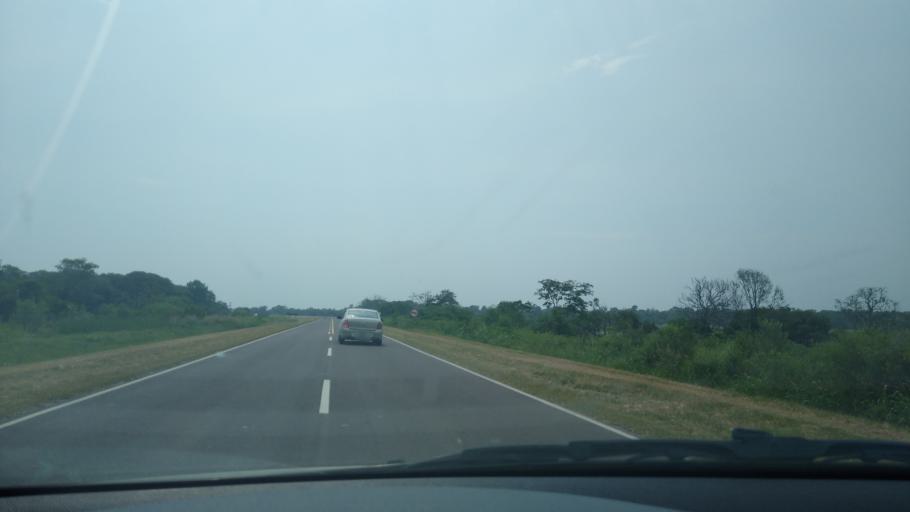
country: AR
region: Chaco
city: La Eduvigis
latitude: -26.8445
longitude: -59.0522
